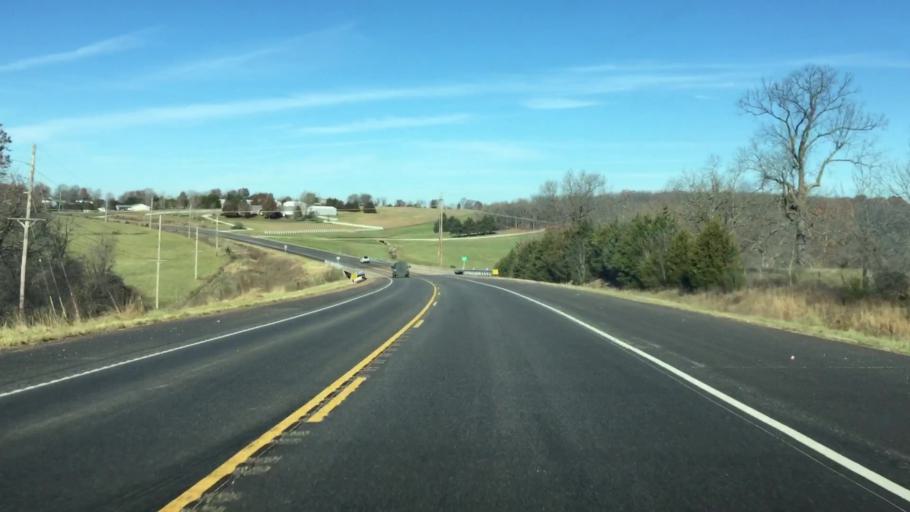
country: US
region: Missouri
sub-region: Miller County
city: Eldon
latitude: 38.3697
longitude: -92.6166
